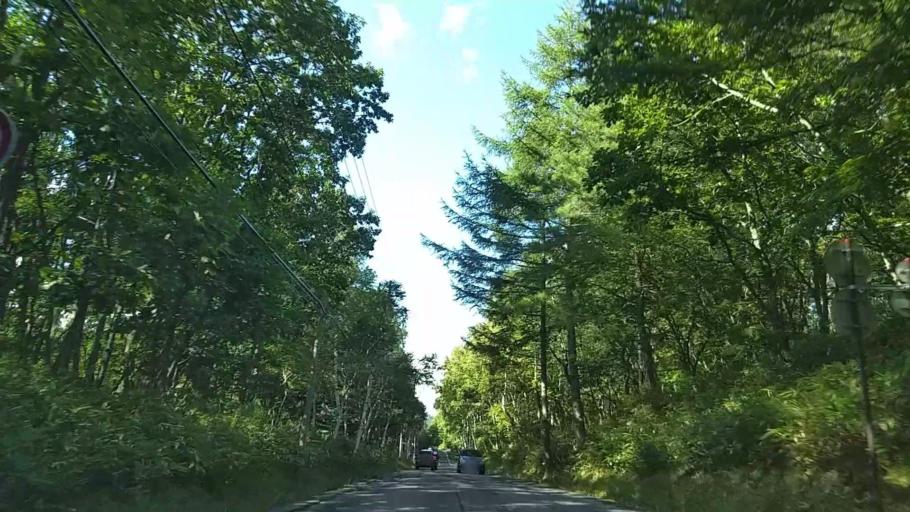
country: JP
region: Nagano
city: Chino
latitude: 36.1029
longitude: 138.2469
